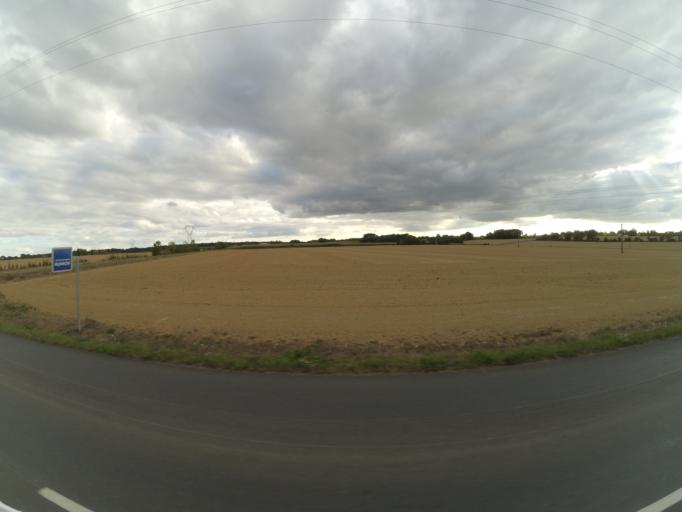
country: FR
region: Pays de la Loire
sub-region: Departement de la Vendee
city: Saint-Andre-Treize-Voies
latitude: 46.9212
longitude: -1.3926
